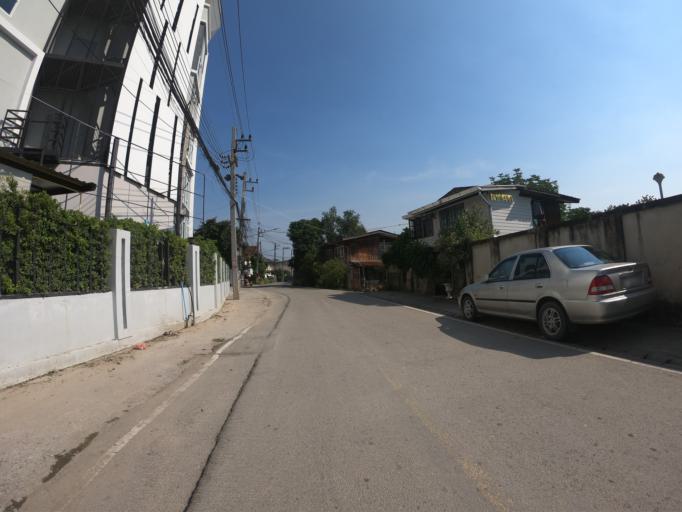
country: TH
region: Chiang Mai
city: Chiang Mai
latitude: 18.8129
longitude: 99.0122
